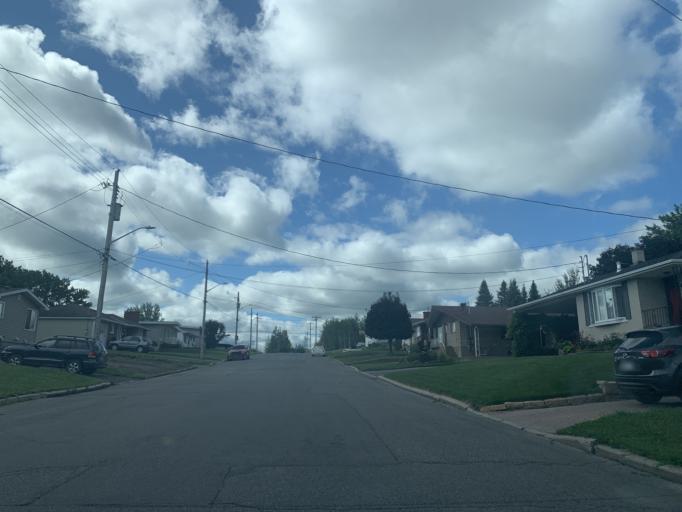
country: CA
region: Ontario
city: Hawkesbury
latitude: 45.6049
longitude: -74.5892
